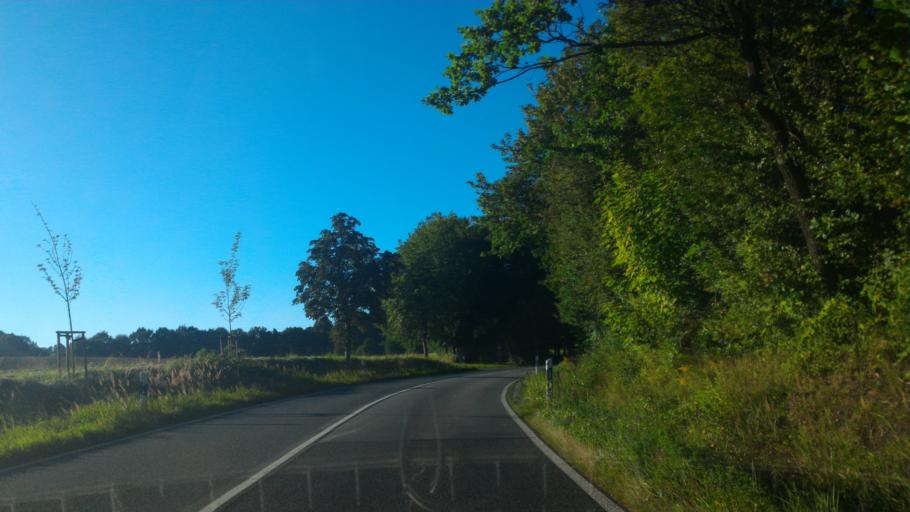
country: DE
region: Saxony
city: Hirschfelde
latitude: 50.9540
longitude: 14.8882
